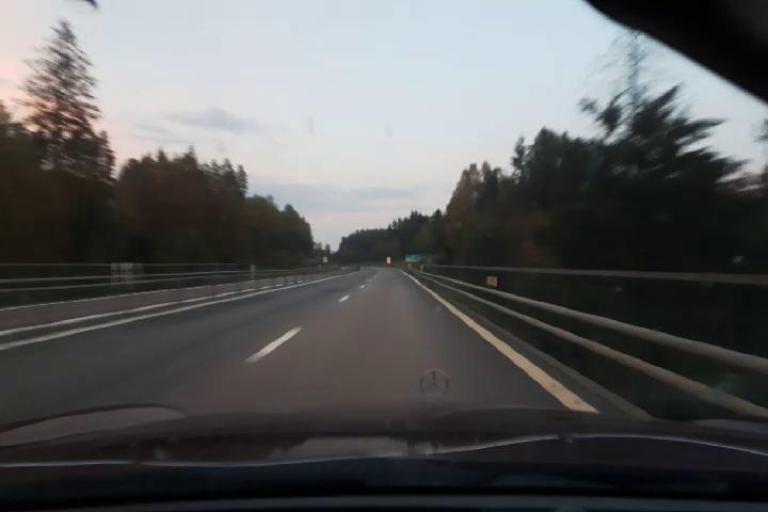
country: SE
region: Vaesternorrland
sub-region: Haernoesands Kommun
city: Haernoesand
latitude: 62.8641
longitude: 18.0347
